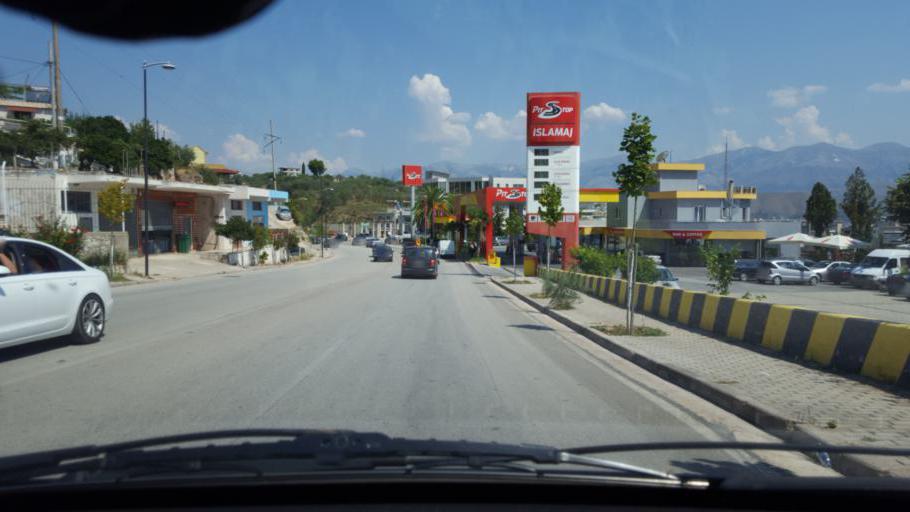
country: AL
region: Vlore
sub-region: Rrethi i Sarandes
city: Sarande
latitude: 39.8723
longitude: 20.0280
